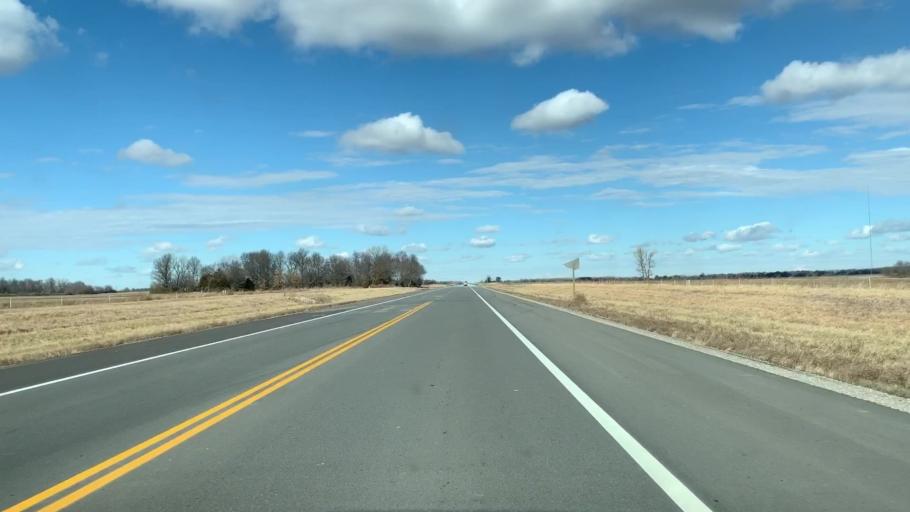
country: US
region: Kansas
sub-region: Cherokee County
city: Columbus
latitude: 37.2866
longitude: -94.8322
